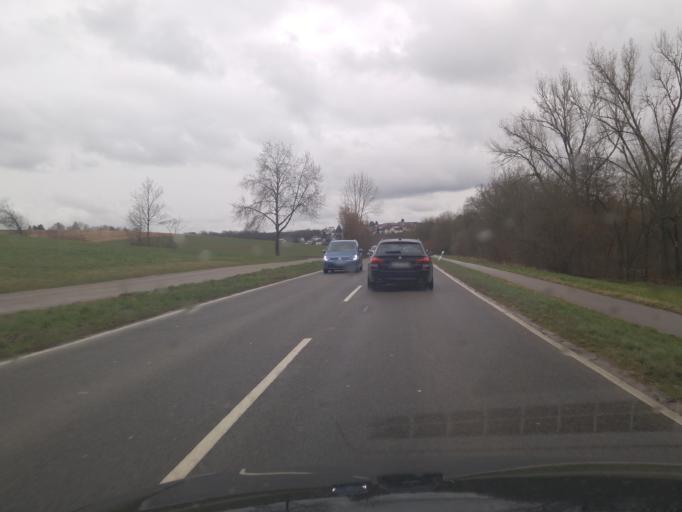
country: DE
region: Baden-Wuerttemberg
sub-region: Regierungsbezirk Stuttgart
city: Steinheim am der Murr
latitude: 48.9571
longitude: 9.2941
